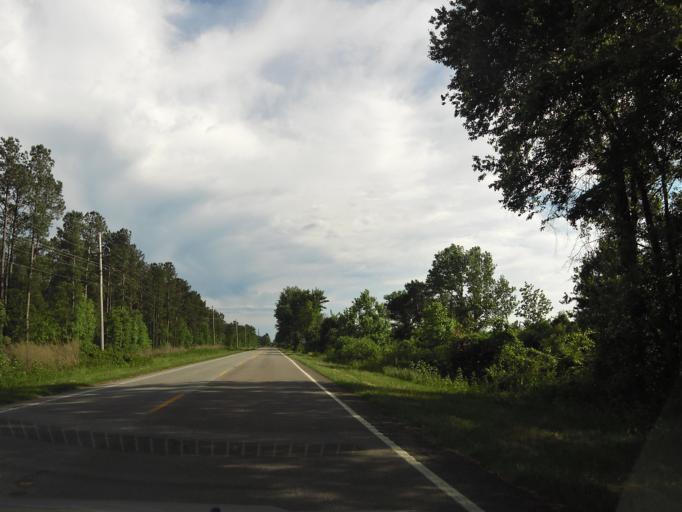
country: US
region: South Carolina
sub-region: Hampton County
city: Estill
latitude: 32.8242
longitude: -81.2397
